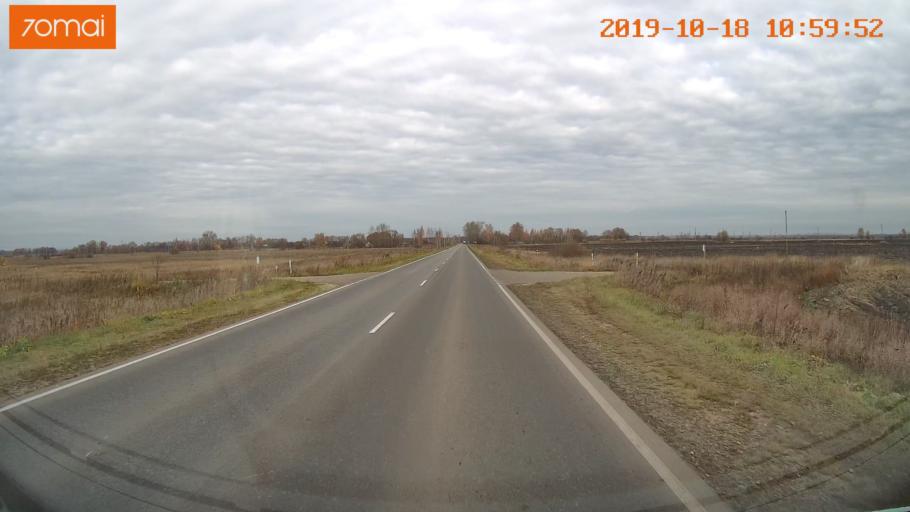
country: RU
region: Tula
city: Yepifan'
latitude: 53.8356
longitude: 38.5550
